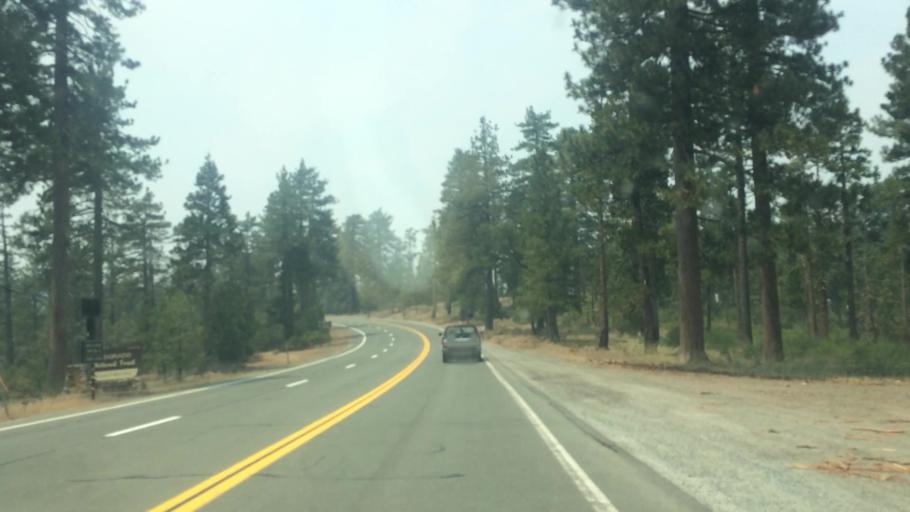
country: US
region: California
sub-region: Amador County
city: Pioneer
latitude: 38.5447
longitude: -120.3714
